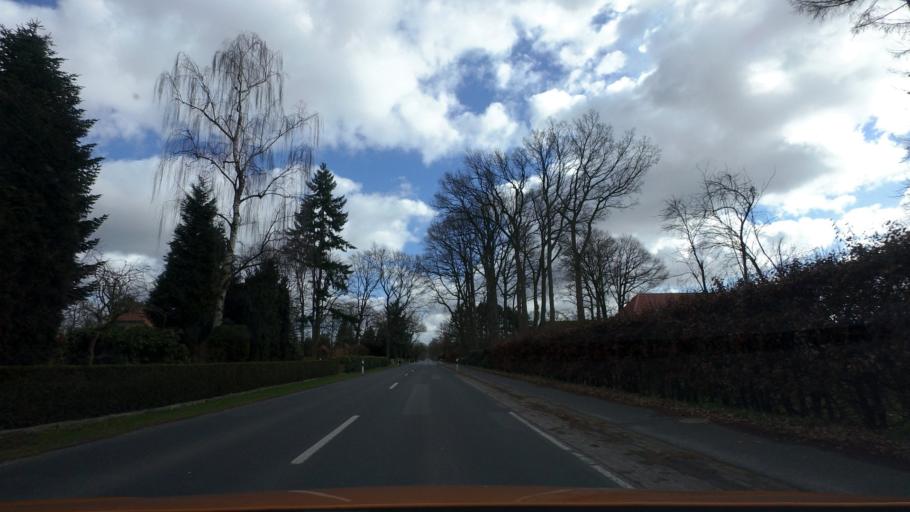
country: DE
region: Lower Saxony
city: Bad Zwischenahn
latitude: 53.1475
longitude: 8.0893
